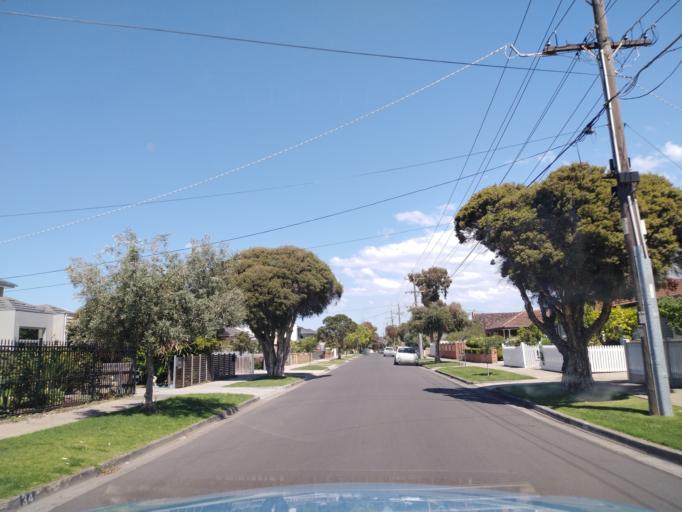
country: AU
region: Victoria
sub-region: Hobsons Bay
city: Altona North
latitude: -37.8368
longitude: 144.8577
